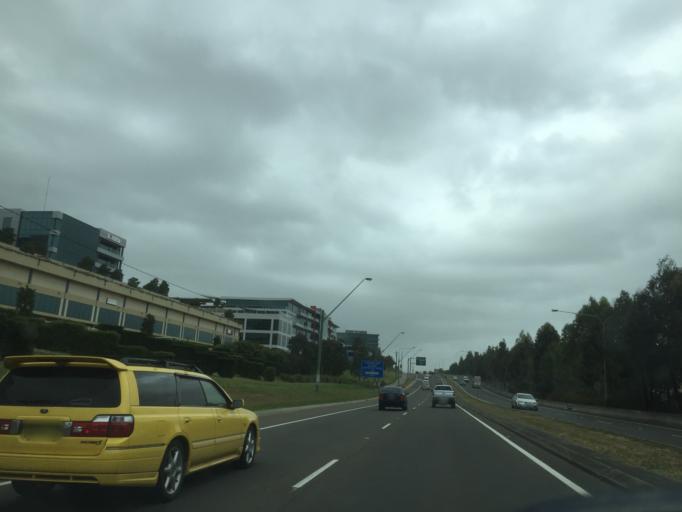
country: AU
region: New South Wales
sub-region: Blacktown
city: Stanhope Gardens
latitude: -33.7348
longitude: 150.9443
